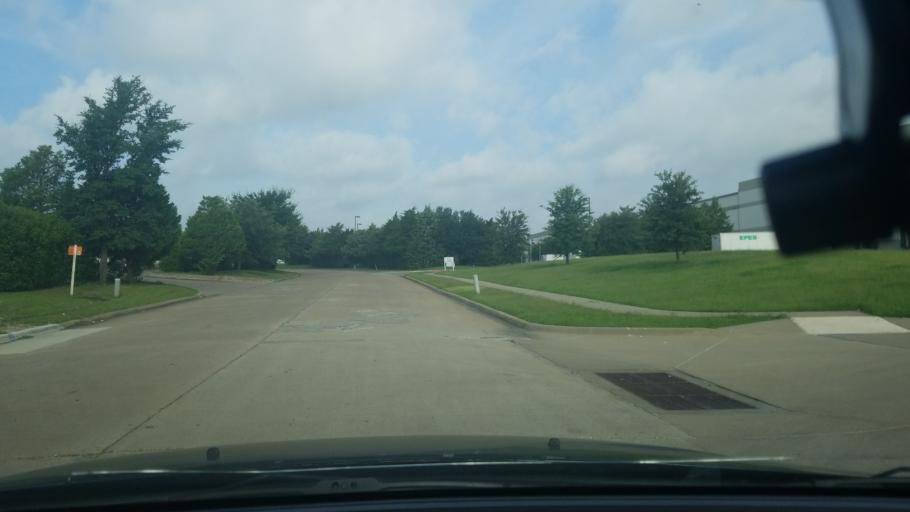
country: US
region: Texas
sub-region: Dallas County
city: Mesquite
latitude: 32.7749
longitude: -96.6496
